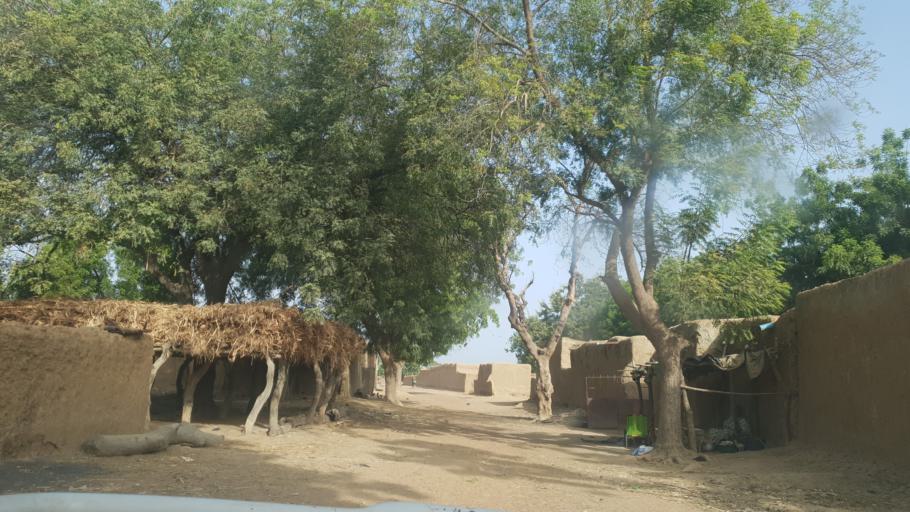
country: ML
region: Segou
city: Baroueli
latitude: 13.3536
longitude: -6.9302
